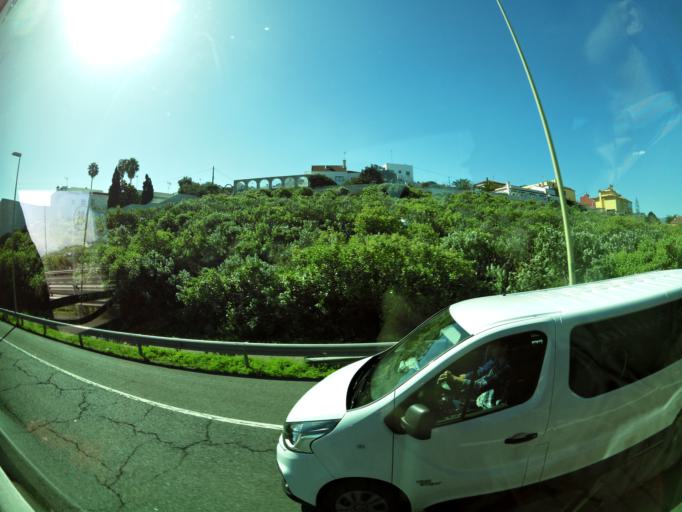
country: ES
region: Canary Islands
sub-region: Provincia de Las Palmas
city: Santa Brigida
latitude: 28.0507
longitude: -15.4573
